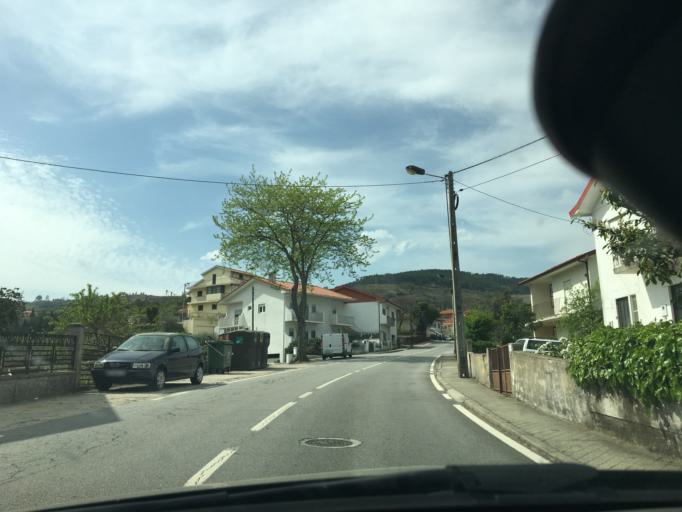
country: PT
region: Vila Real
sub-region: Boticas
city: Boticas
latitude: 41.6866
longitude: -7.6722
